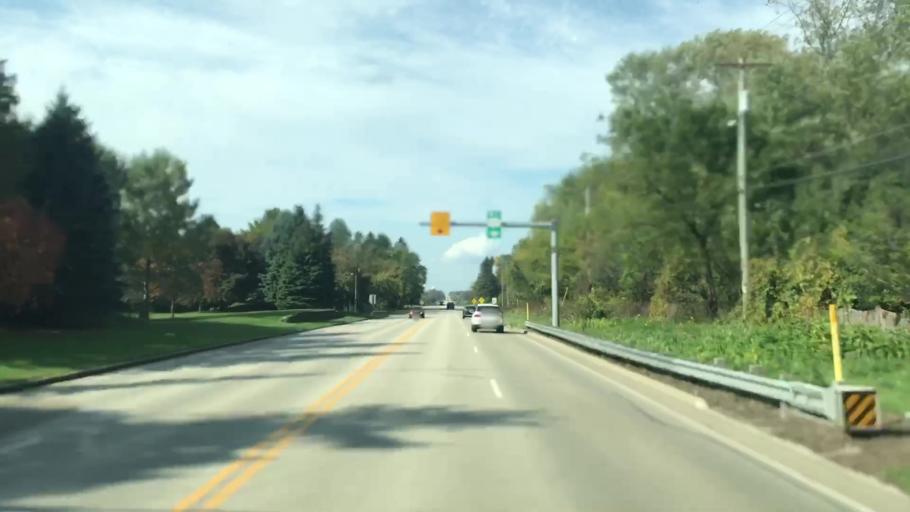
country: US
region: Wisconsin
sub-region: Ozaukee County
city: Mequon
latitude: 43.2216
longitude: -88.0167
